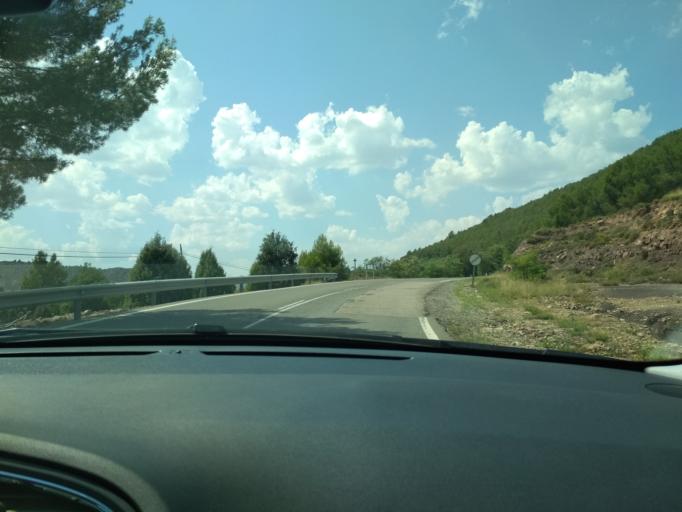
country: ES
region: Aragon
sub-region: Provincia de Teruel
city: Rubielos de Mora
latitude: 40.1838
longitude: -0.6435
